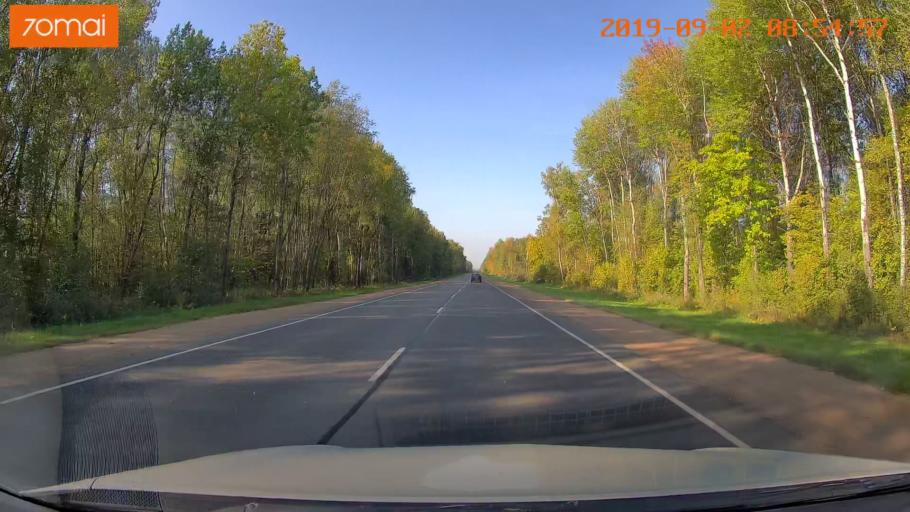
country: RU
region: Kaluga
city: Medyn'
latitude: 54.9575
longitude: 35.8276
